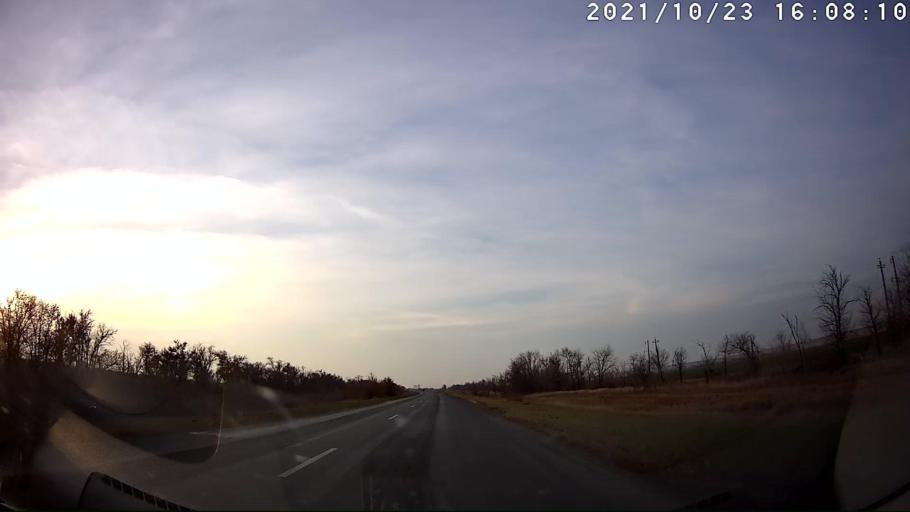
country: RU
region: Volgograd
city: Kotel'nikovo
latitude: 47.9391
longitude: 43.7231
